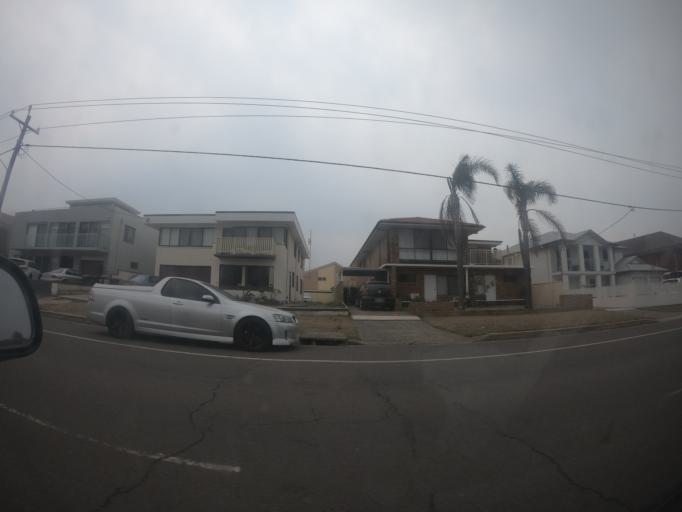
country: AU
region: New South Wales
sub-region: Shellharbour
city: Lake Illawarra
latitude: -34.5484
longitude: 150.8690
